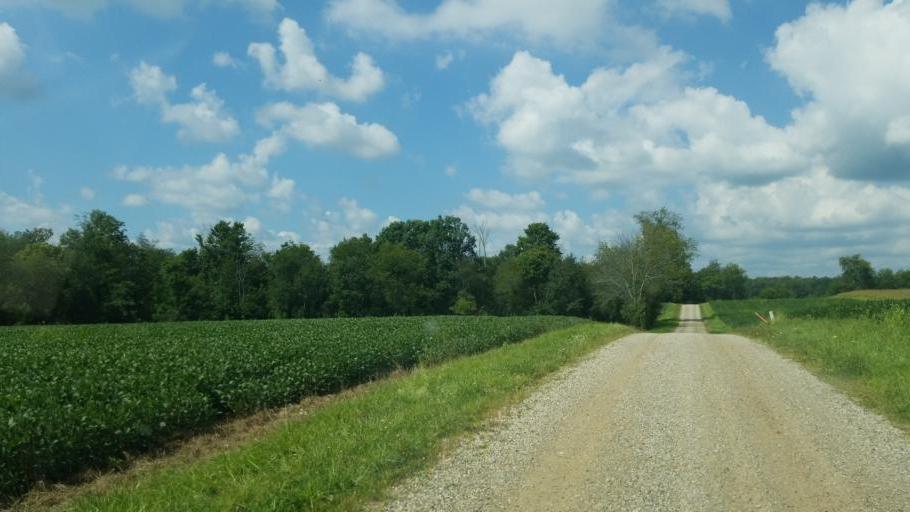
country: US
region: Ohio
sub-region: Knox County
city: Oak Hill
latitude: 40.3838
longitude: -82.3104
